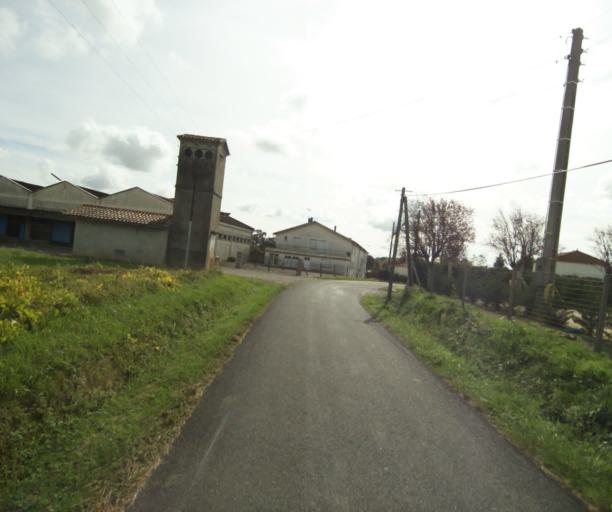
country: FR
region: Midi-Pyrenees
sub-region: Departement du Gers
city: Eauze
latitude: 43.8592
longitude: 0.0814
